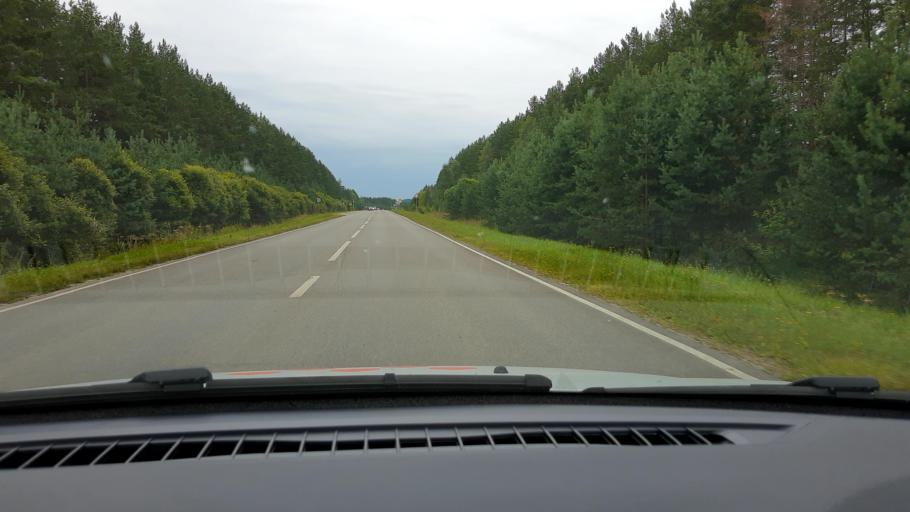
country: RU
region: Nizjnij Novgorod
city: Vyyezdnoye
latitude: 55.1986
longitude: 43.6203
